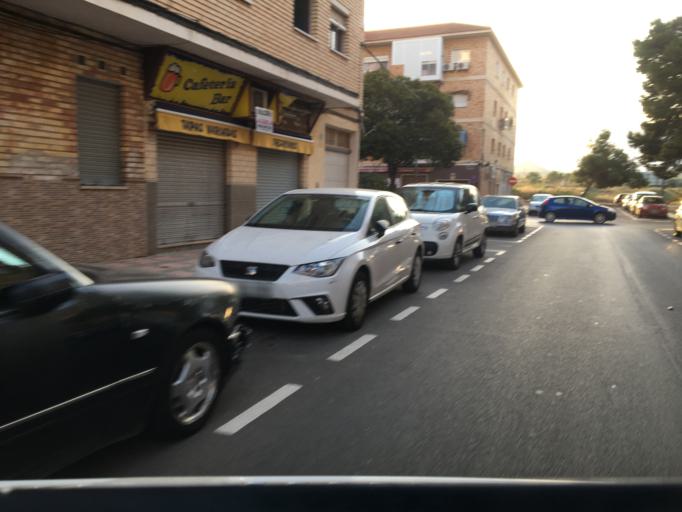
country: ES
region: Murcia
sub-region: Murcia
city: Cartagena
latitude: 37.6241
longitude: -0.9836
